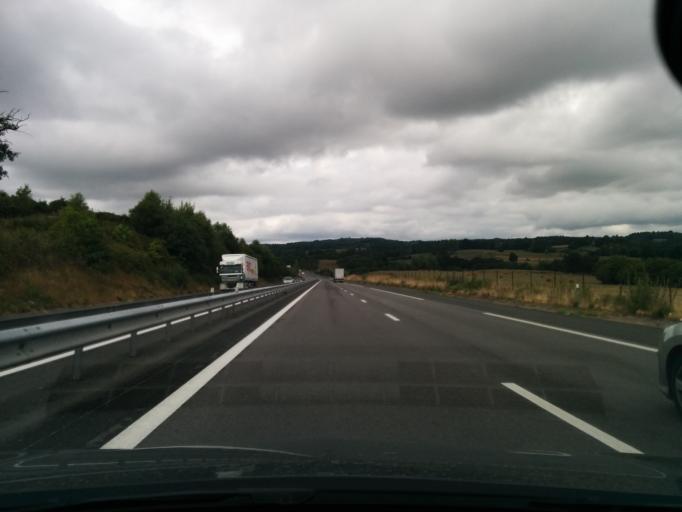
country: FR
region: Limousin
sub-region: Departement de la Correze
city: Vigeois
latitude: 45.3323
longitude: 1.5722
